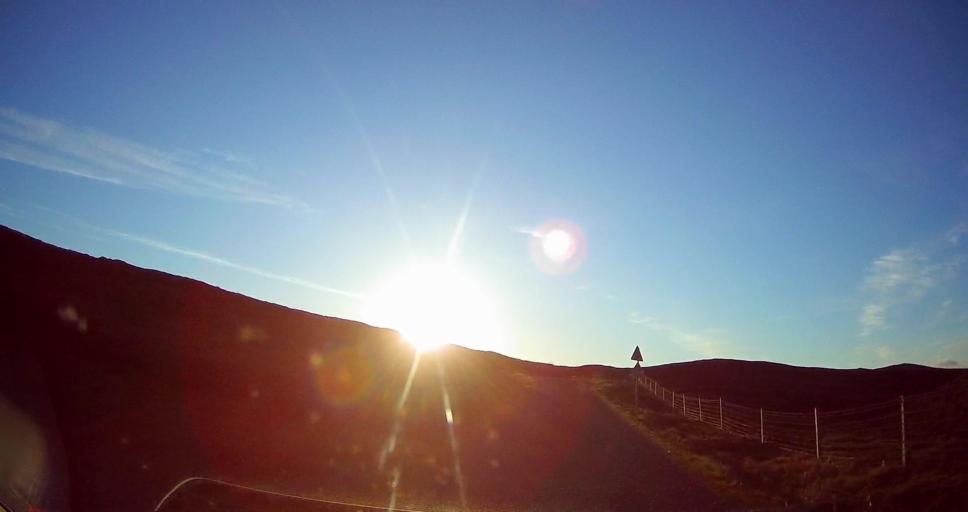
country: GB
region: Scotland
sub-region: Shetland Islands
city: Lerwick
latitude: 60.4398
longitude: -1.3984
